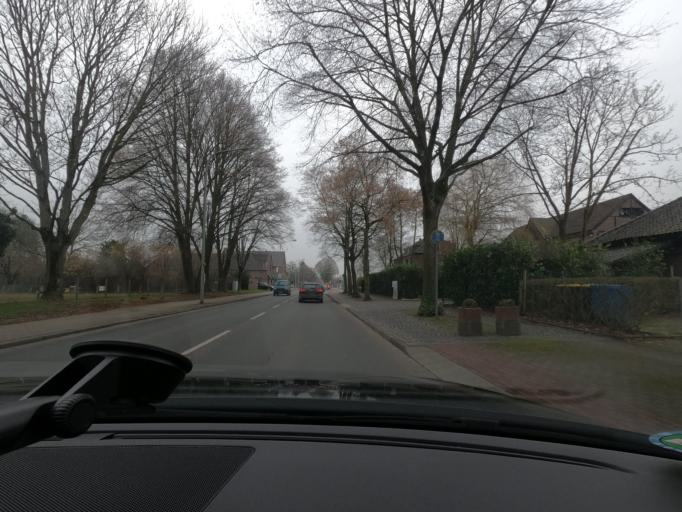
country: DE
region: North Rhine-Westphalia
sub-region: Regierungsbezirk Dusseldorf
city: Krefeld
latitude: 51.3625
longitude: 6.5699
